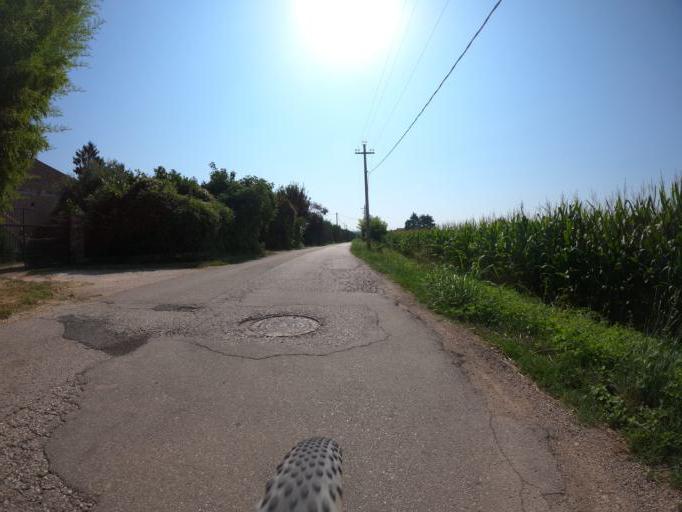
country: IT
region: Veneto
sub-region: Provincia di Verona
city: Costermano
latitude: 45.5856
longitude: 10.7648
